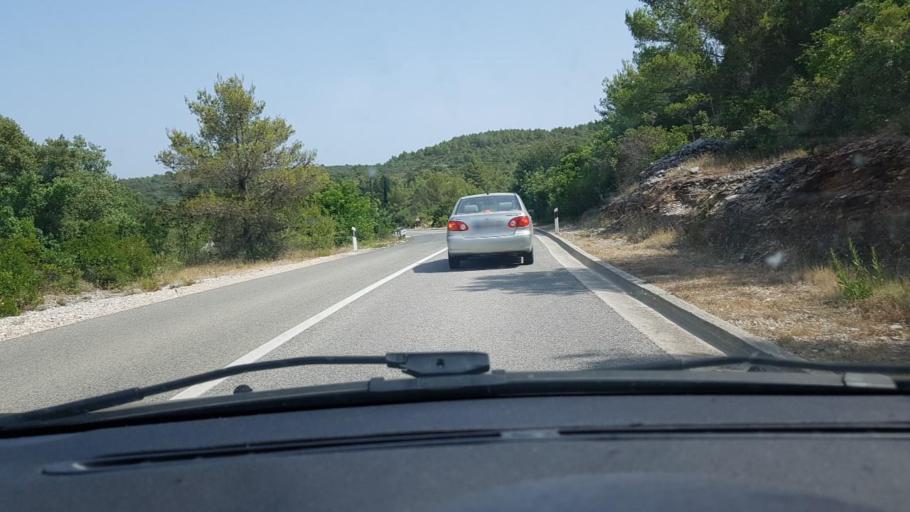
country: HR
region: Dubrovacko-Neretvanska
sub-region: Grad Korcula
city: Zrnovo
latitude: 42.9380
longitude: 17.0789
